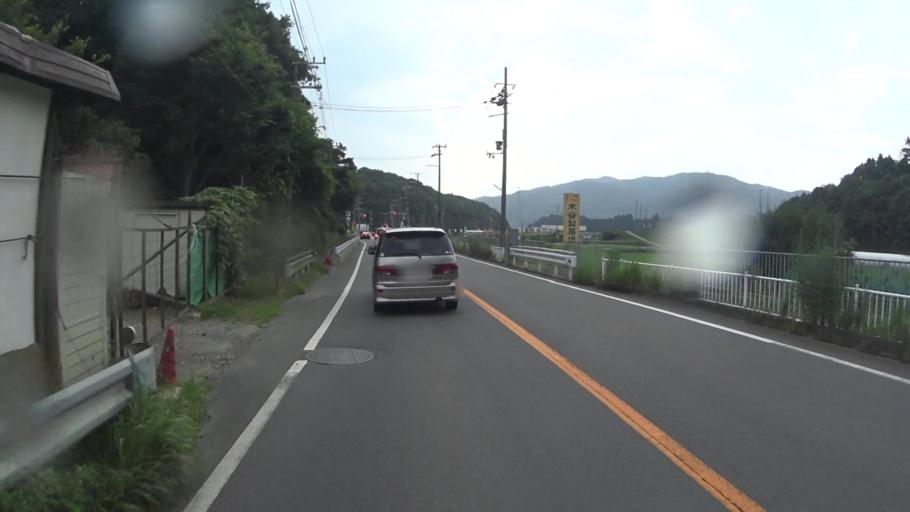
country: JP
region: Kyoto
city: Uji
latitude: 34.8577
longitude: 135.8900
